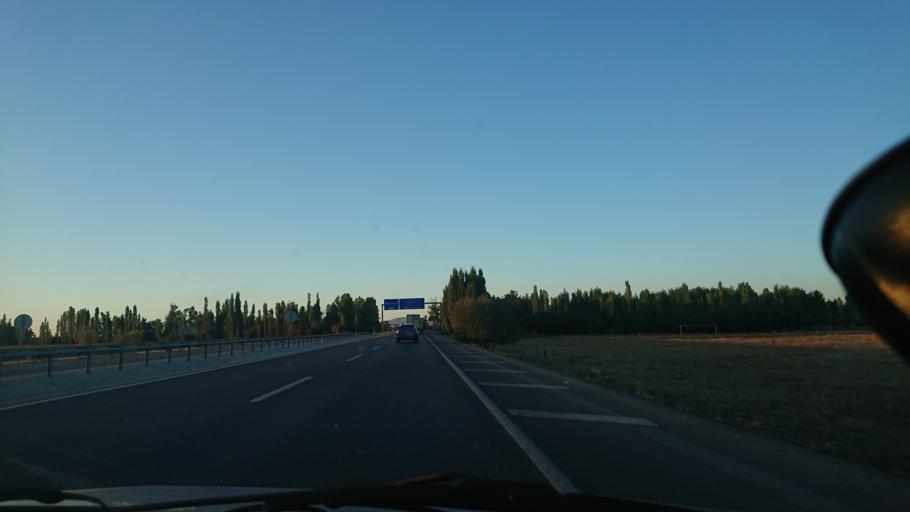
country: TR
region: Eskisehir
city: Mahmudiye
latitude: 39.5670
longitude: 30.9142
